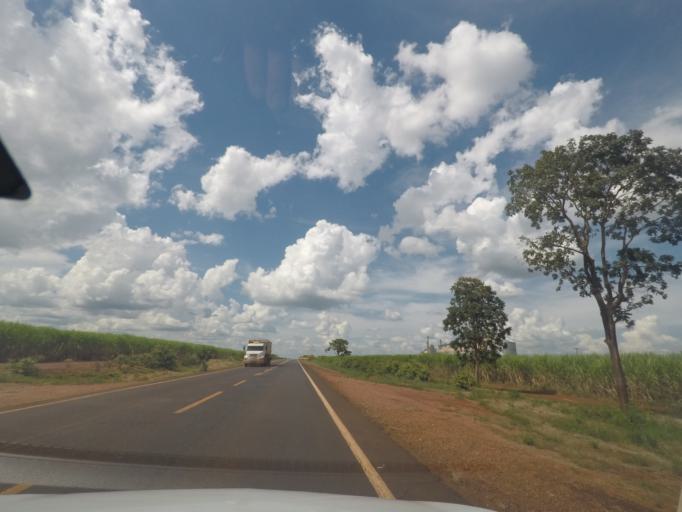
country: BR
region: Minas Gerais
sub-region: Conceicao Das Alagoas
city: Conceicao das Alagoas
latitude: -19.8094
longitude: -48.5827
